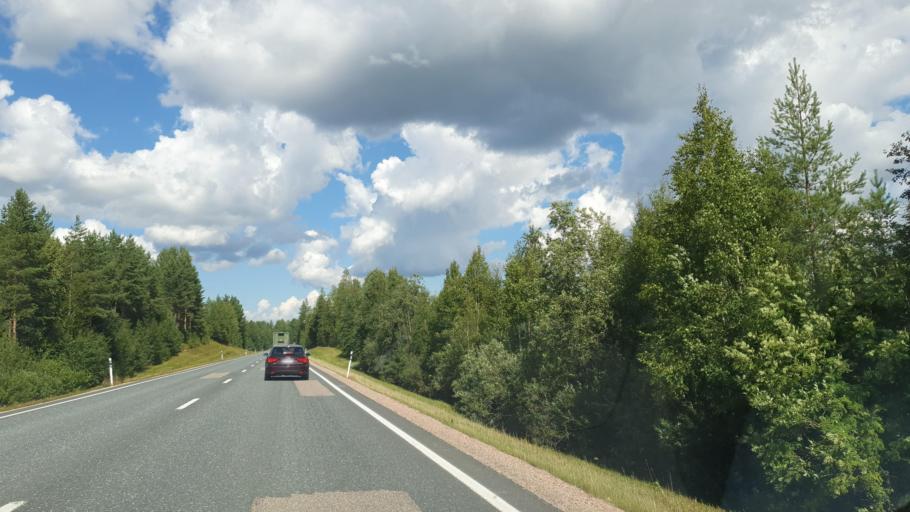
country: FI
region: Kainuu
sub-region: Kajaani
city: Kajaani
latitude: 64.1040
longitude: 27.4488
